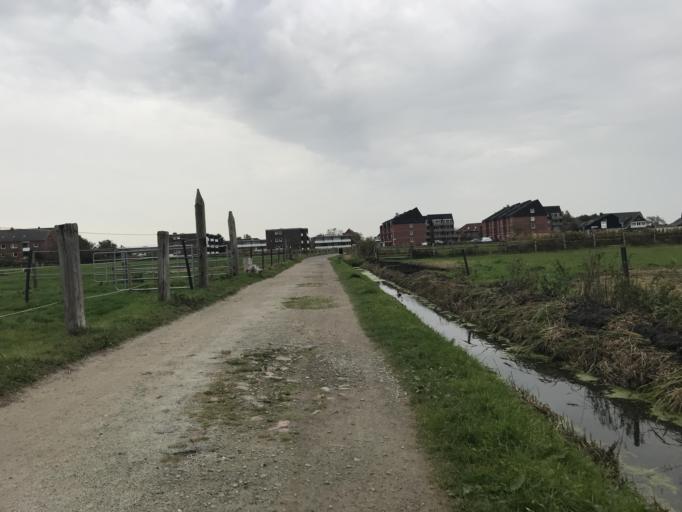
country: DE
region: Lower Saxony
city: Borkum
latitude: 53.5910
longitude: 6.6705
